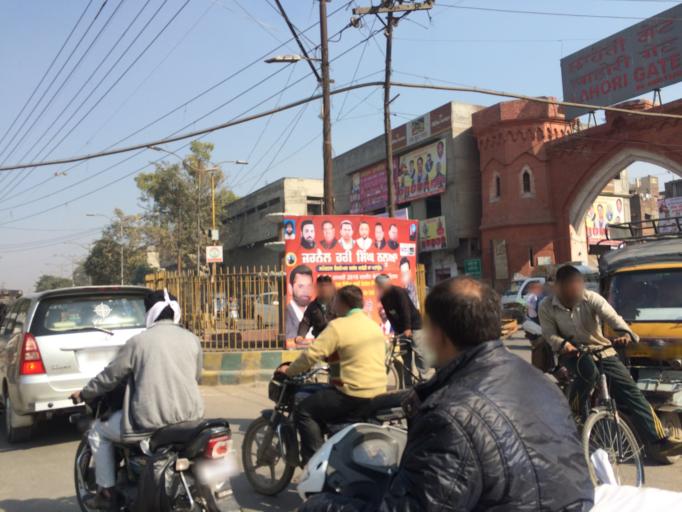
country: IN
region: Punjab
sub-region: Amritsar
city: Amritsar
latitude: 31.6195
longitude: 74.8641
